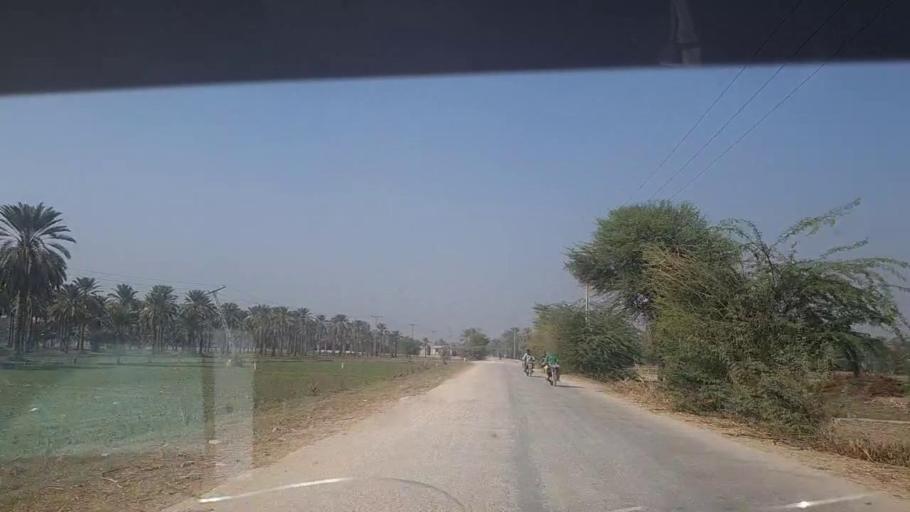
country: PK
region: Sindh
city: Kot Diji
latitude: 27.3608
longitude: 68.7080
